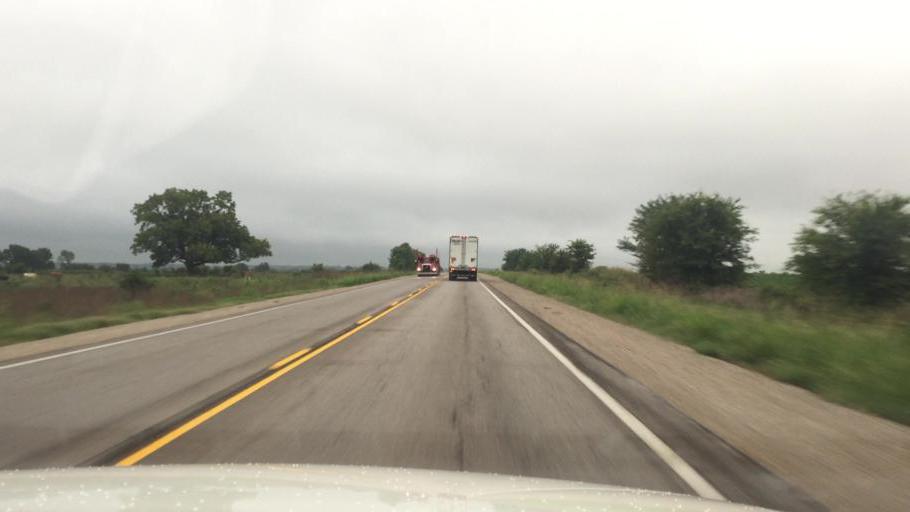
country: US
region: Kansas
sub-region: Montgomery County
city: Cherryvale
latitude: 37.2017
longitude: -95.5837
